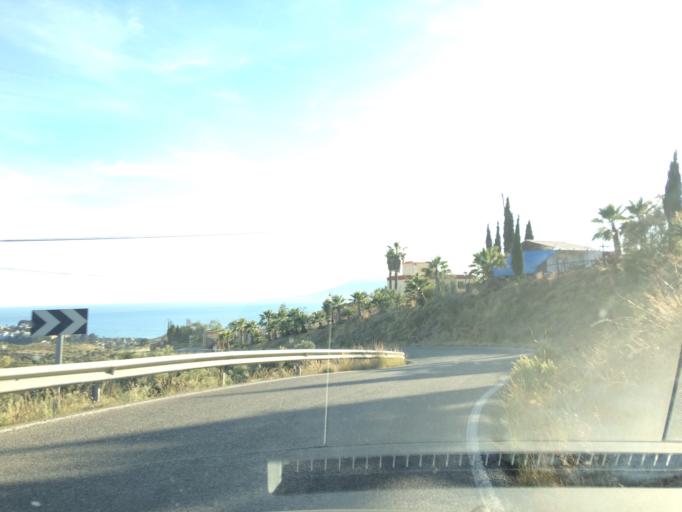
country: ES
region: Andalusia
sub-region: Provincia de Malaga
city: Totalan
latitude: 36.7344
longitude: -4.3360
